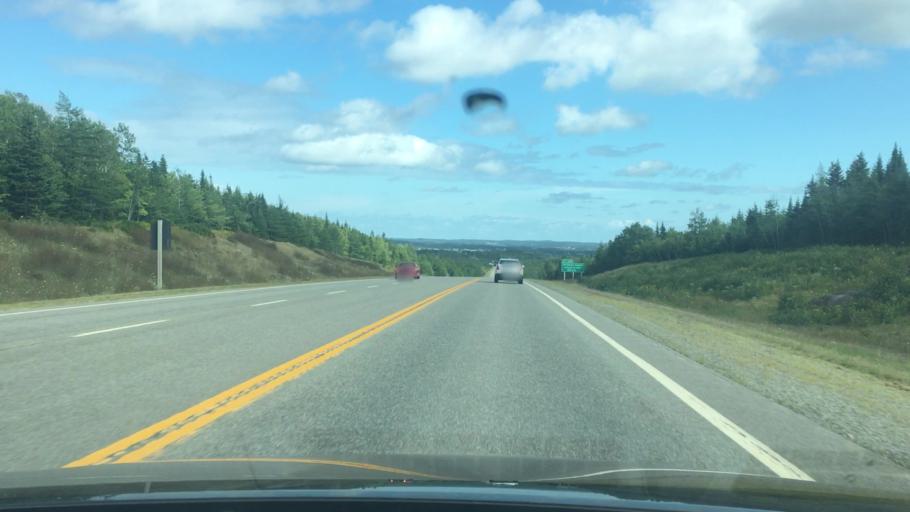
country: CA
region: Nova Scotia
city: Port Hawkesbury
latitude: 45.6212
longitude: -61.1180
